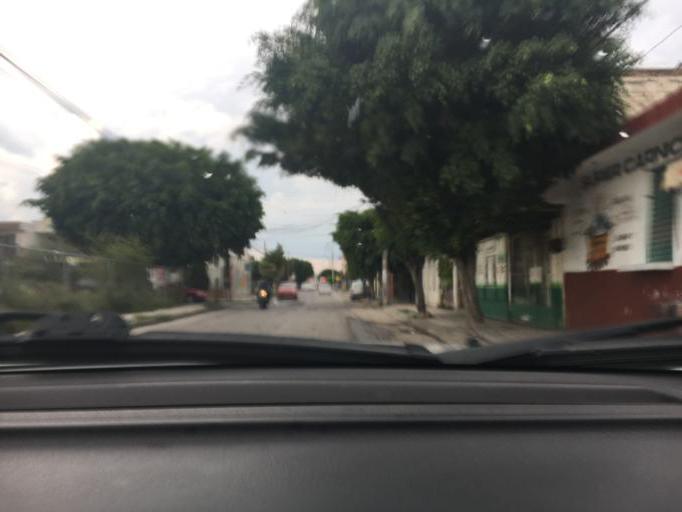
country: MX
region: Guanajuato
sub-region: Leon
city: San Jose de Duran (Los Troncoso)
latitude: 21.0803
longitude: -101.6538
